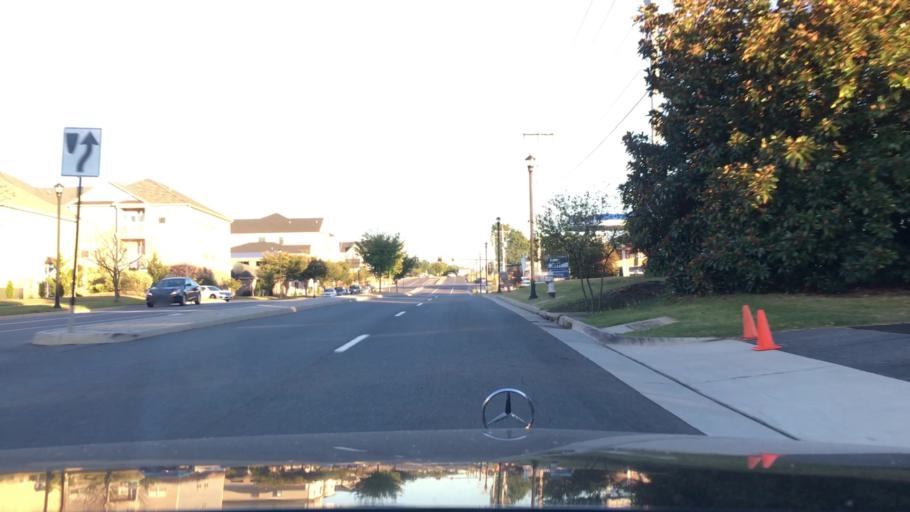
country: US
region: Virginia
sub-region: Campbell County
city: Timberlake
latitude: 37.3402
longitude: -79.2273
